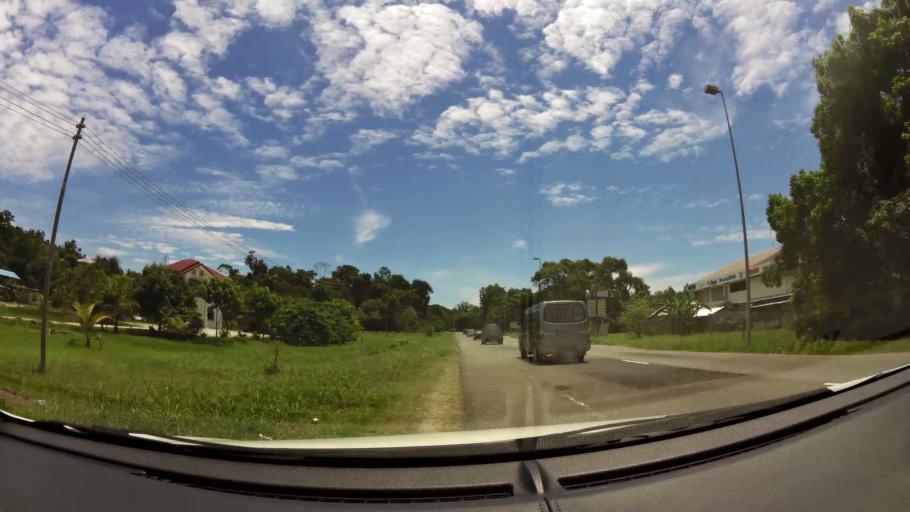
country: BN
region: Brunei and Muara
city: Bandar Seri Begawan
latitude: 5.0056
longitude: 115.0290
